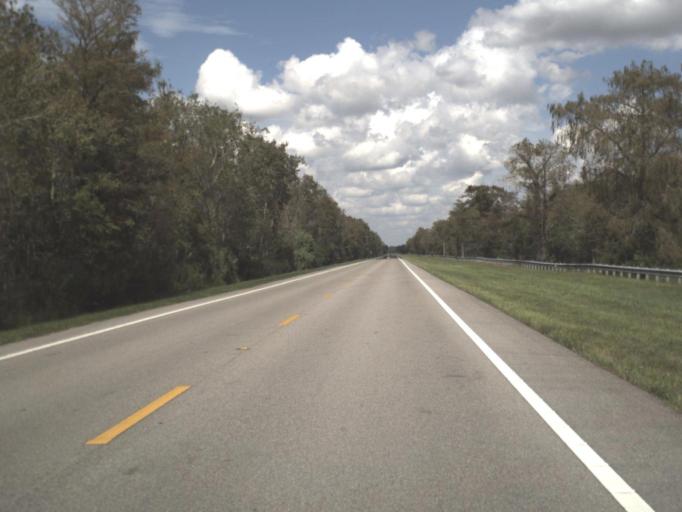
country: US
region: Florida
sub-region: Collier County
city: Immokalee
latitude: 26.2319
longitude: -81.3436
